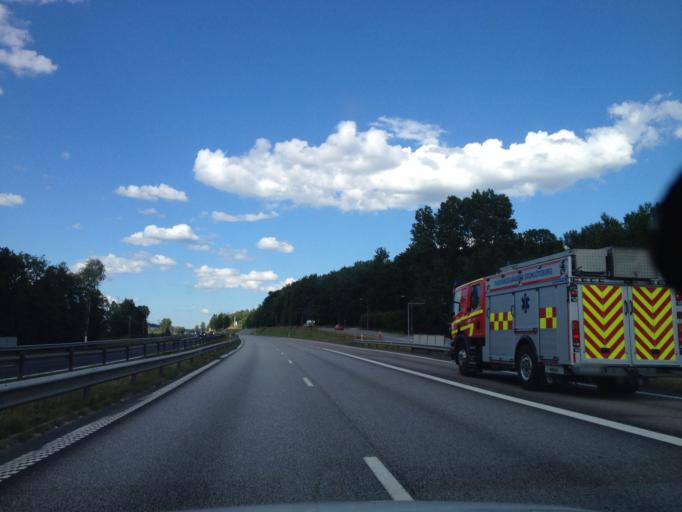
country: SE
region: Vaestra Goetaland
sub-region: Lerums Kommun
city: Lerum
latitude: 57.7541
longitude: 12.2491
